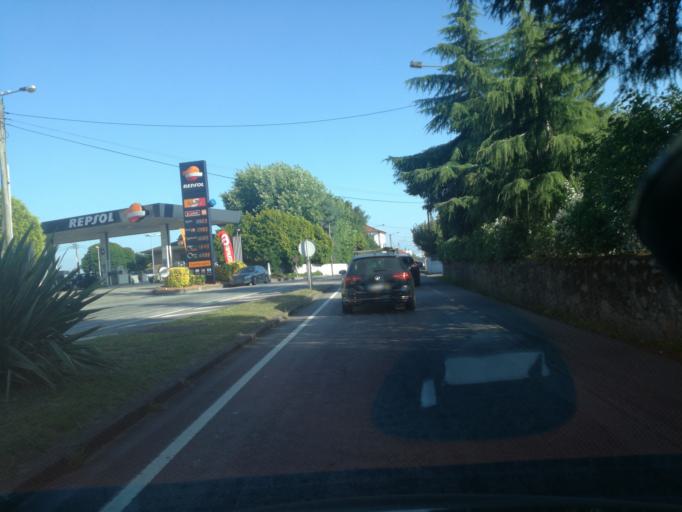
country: PT
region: Porto
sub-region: Maia
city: Gemunde
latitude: 41.2488
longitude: -8.6493
